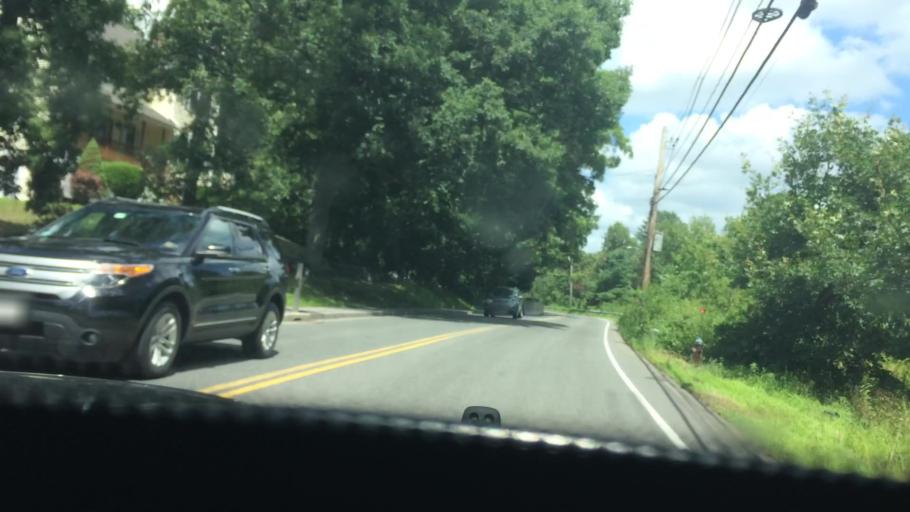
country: US
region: Massachusetts
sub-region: Middlesex County
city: Maynard
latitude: 42.4124
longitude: -71.4455
